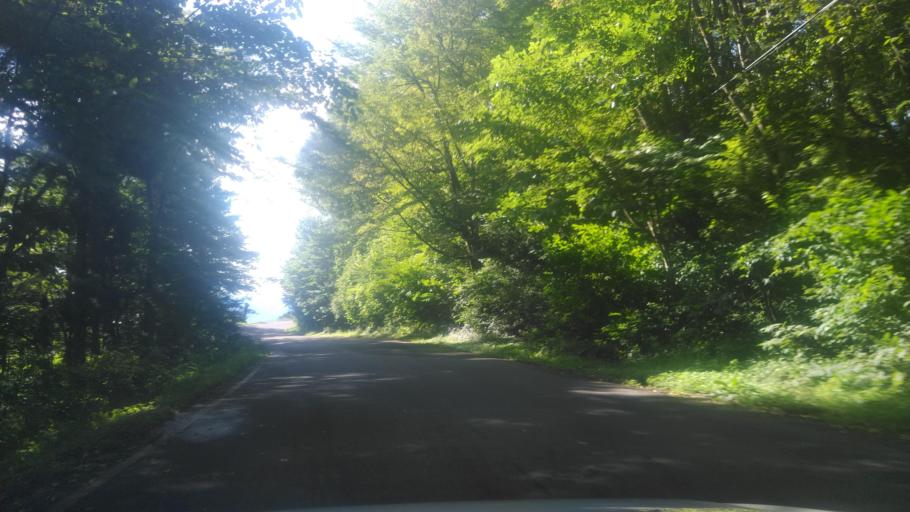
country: JP
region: Nagano
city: Nagano-shi
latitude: 36.7868
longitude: 138.1778
